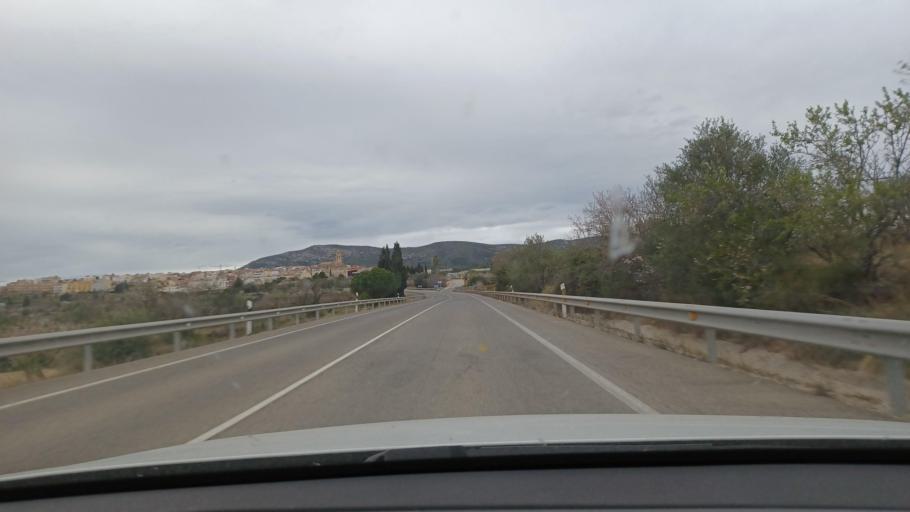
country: ES
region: Valencia
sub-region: Provincia de Castello
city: Traiguera
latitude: 40.5236
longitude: 0.3021
